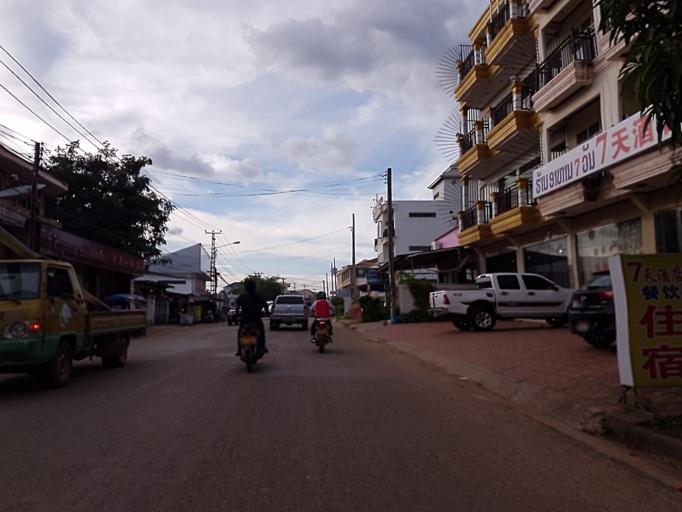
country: LA
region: Vientiane
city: Vientiane
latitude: 17.9794
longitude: 102.5869
